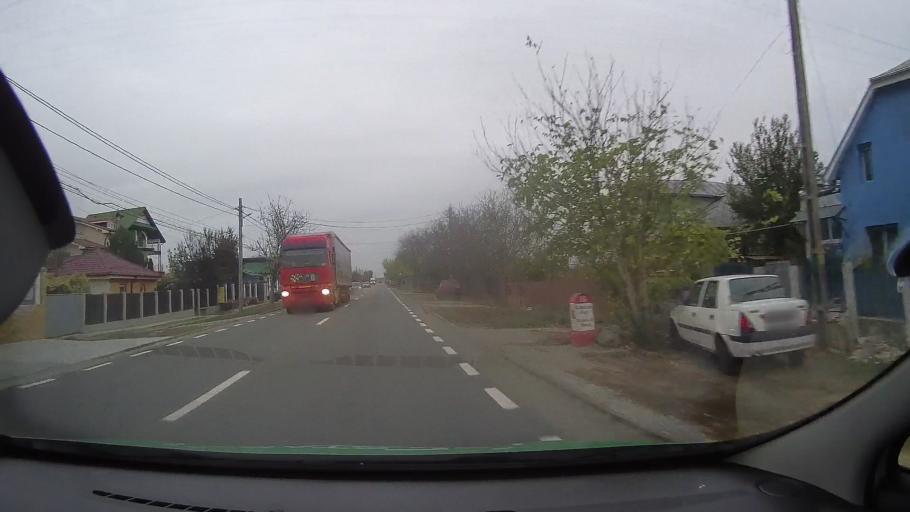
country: RO
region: Ialomita
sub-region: Comuna Slobozia
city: Slobozia
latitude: 44.5991
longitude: 27.3891
